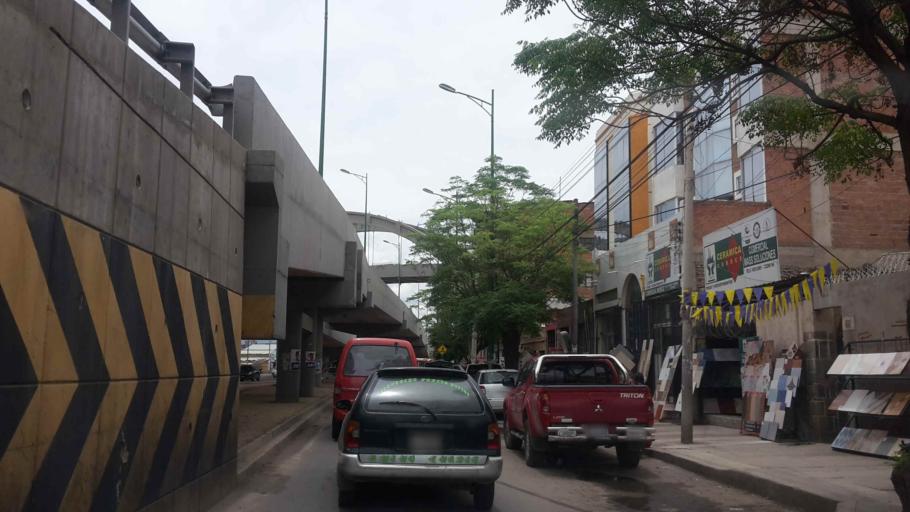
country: BO
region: Cochabamba
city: Cochabamba
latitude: -17.4114
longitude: -66.1527
